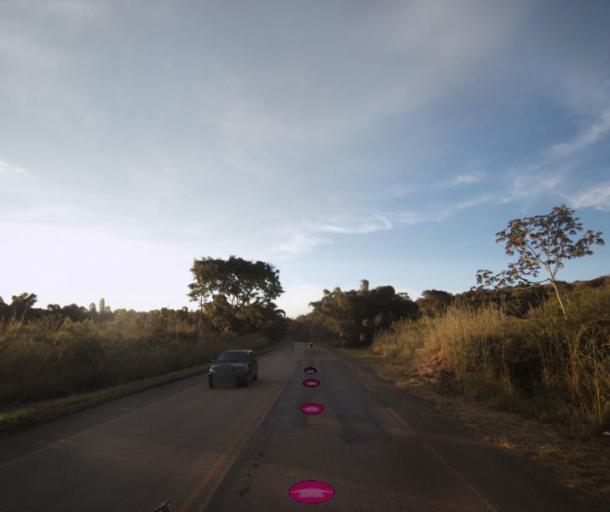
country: BR
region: Goias
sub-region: Abadiania
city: Abadiania
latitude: -16.1332
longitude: -48.8929
